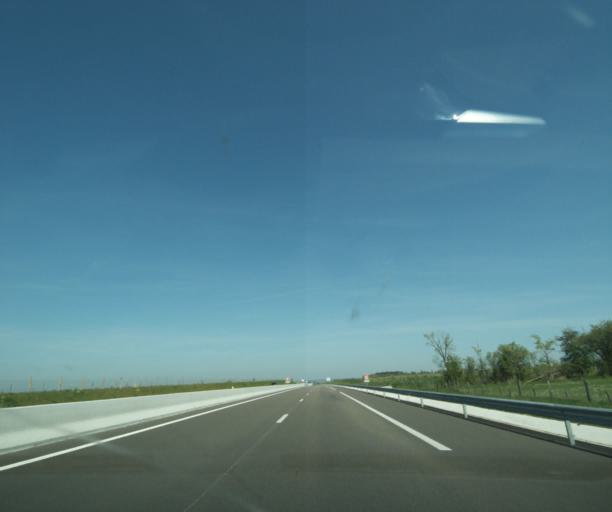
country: FR
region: Bourgogne
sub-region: Departement de la Nievre
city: Saint-Pierre-le-Moutier
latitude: 46.8056
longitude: 3.1208
